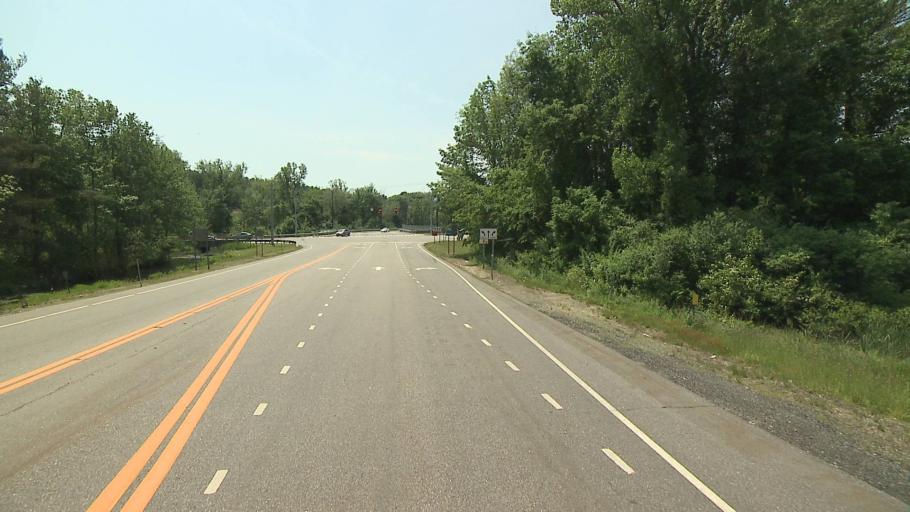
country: US
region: Connecticut
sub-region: Windham County
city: Putnam
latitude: 41.9251
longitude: -71.8863
